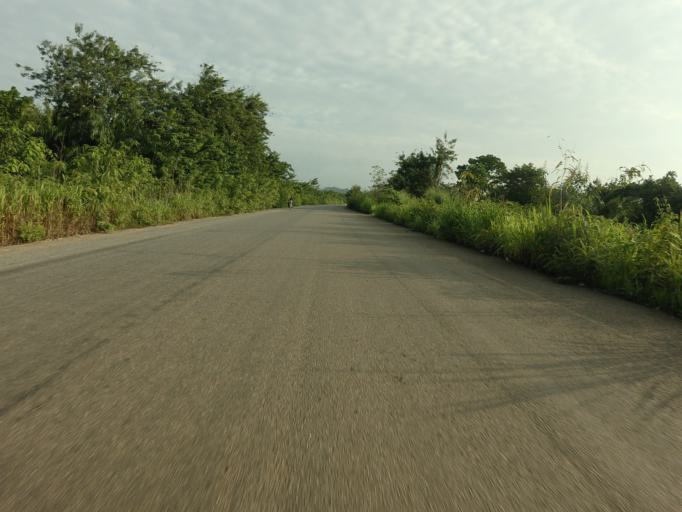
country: GH
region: Volta
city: Kpandu
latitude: 6.9088
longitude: 0.4455
